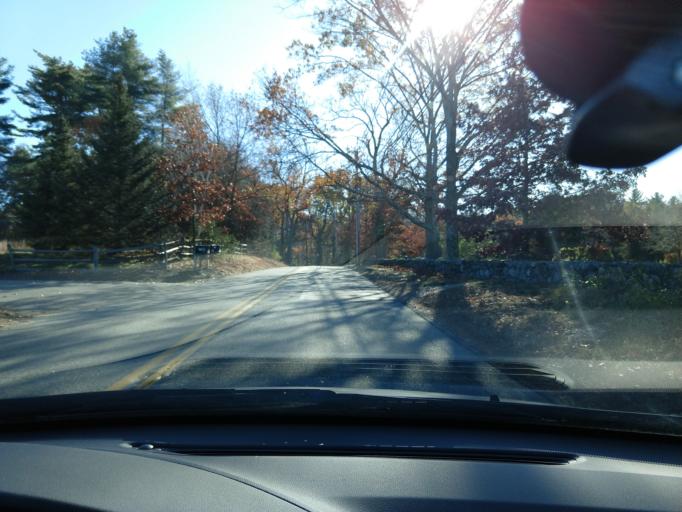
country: US
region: Massachusetts
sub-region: Middlesex County
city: Concord
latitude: 42.4937
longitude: -71.3329
